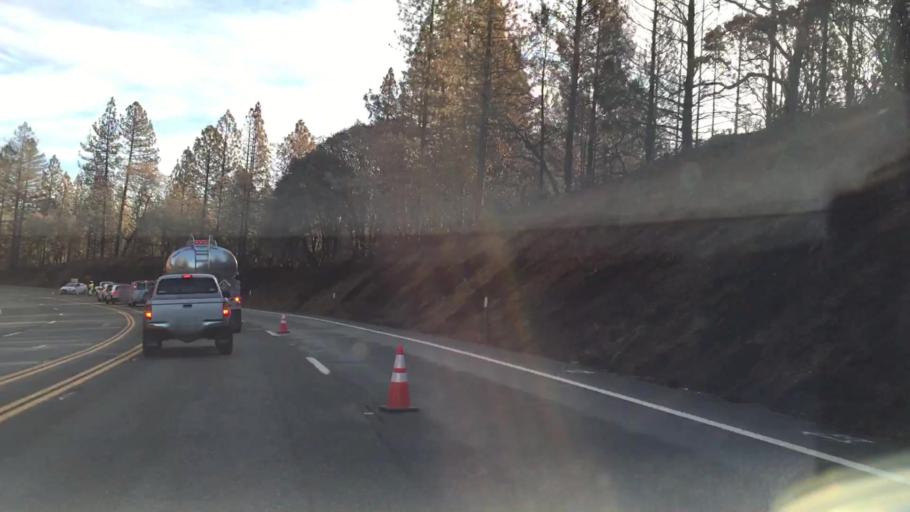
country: US
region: California
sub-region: Butte County
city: Paradise
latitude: 39.7104
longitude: -121.5259
